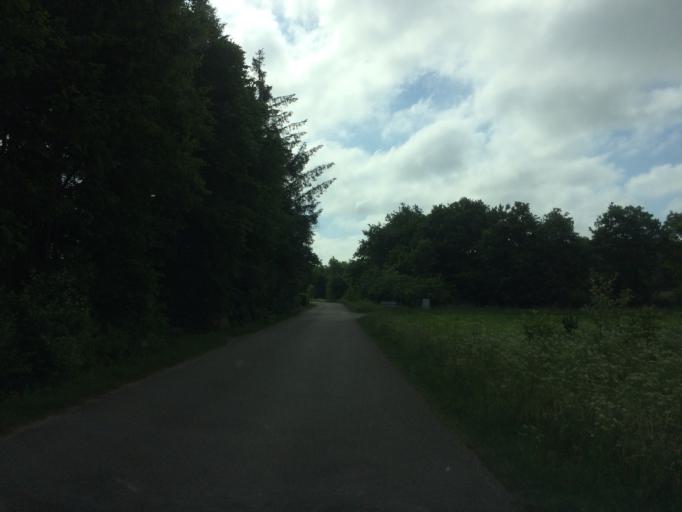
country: DK
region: Central Jutland
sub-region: Holstebro Kommune
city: Ulfborg
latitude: 56.2365
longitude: 8.4226
